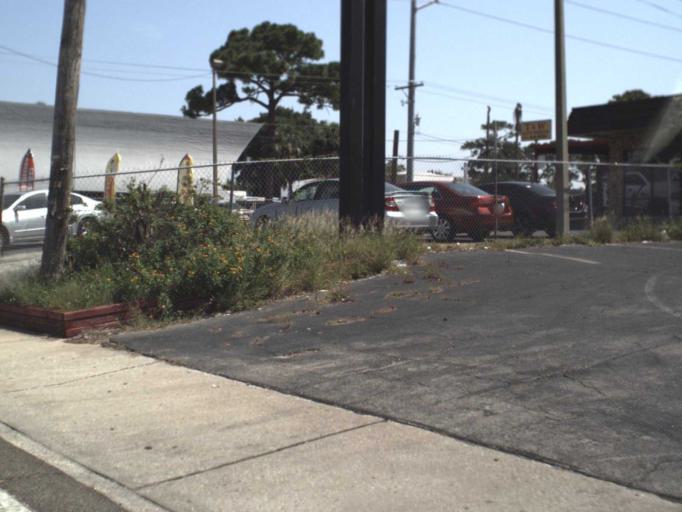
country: US
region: Florida
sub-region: Hillsborough County
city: Lake Magdalene
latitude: 28.0432
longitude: -82.4594
